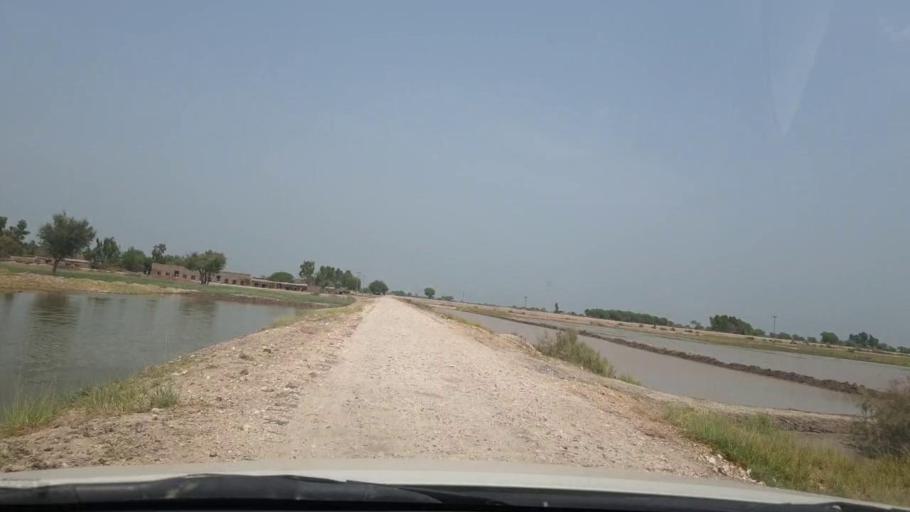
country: PK
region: Sindh
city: Rustam jo Goth
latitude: 28.0760
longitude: 68.8180
